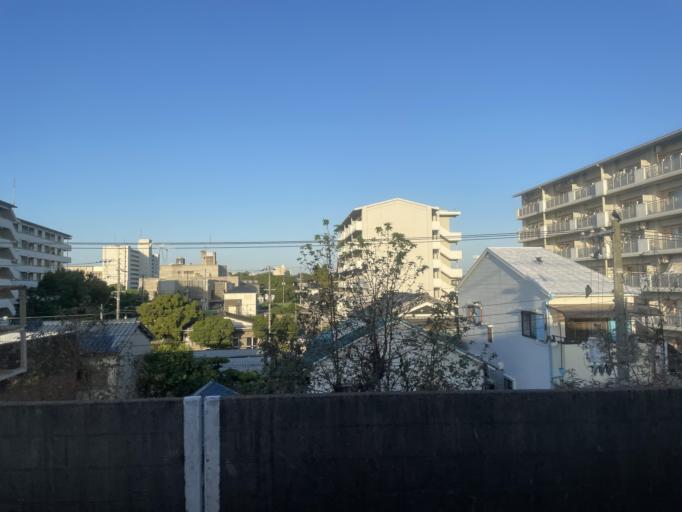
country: JP
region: Osaka
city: Matsubara
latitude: 34.6000
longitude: 135.5322
